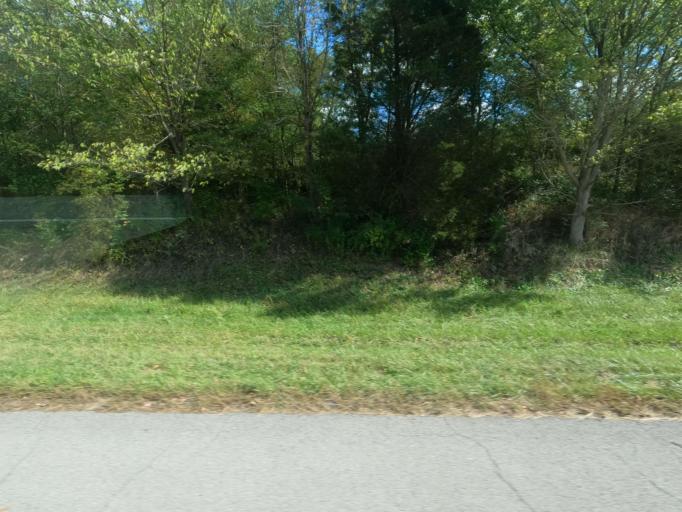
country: US
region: Illinois
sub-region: Johnson County
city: Vienna
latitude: 37.4411
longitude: -88.8924
